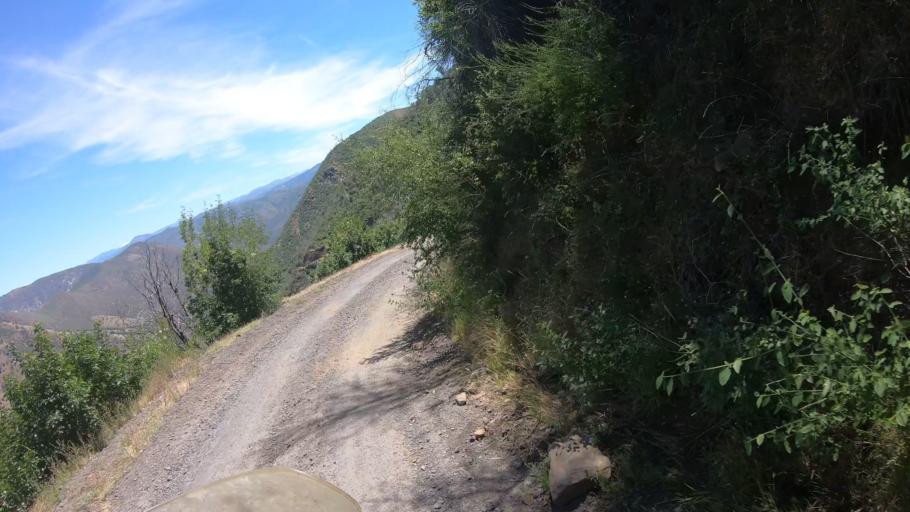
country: US
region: California
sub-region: Tuolumne County
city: Tuolumne City
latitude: 37.8317
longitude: -120.1081
